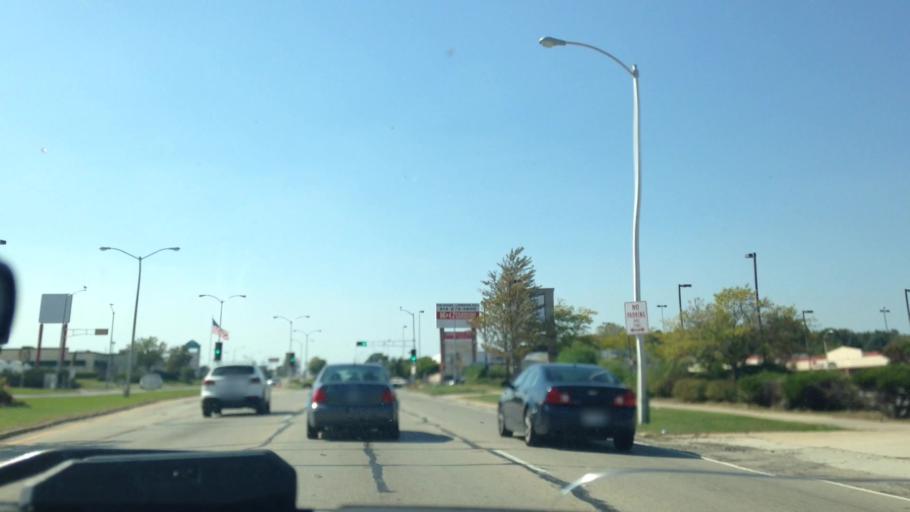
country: US
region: Wisconsin
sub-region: Milwaukee County
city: Brown Deer
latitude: 43.1779
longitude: -88.0144
